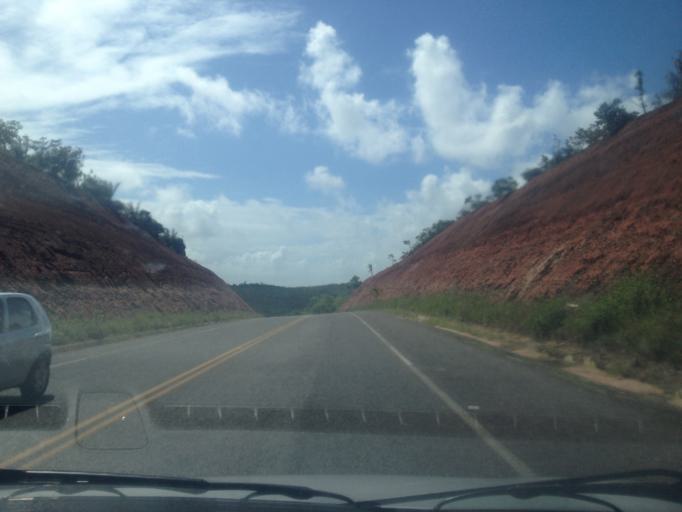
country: BR
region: Bahia
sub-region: Conde
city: Conde
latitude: -11.9121
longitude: -37.6584
